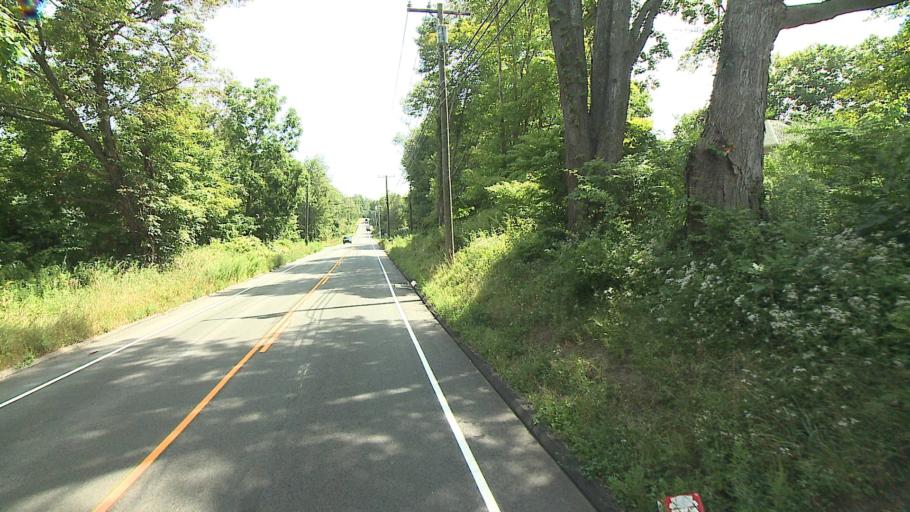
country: US
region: Connecticut
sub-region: Litchfield County
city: Bethlehem Village
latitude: 41.6123
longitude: -73.1899
